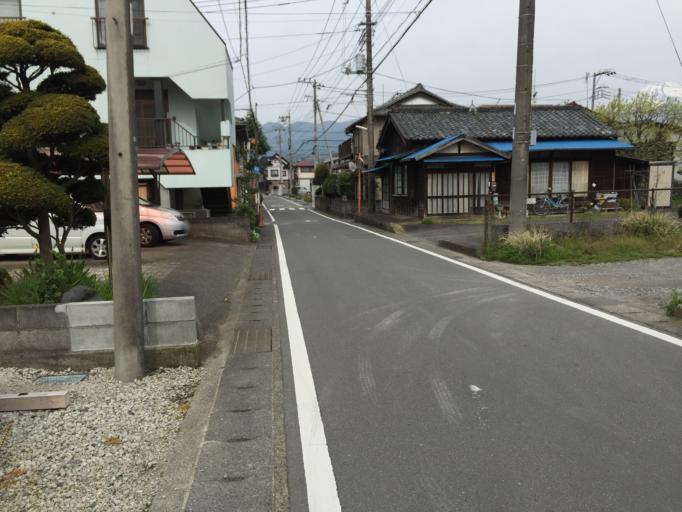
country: JP
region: Shizuoka
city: Mishima
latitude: 35.1716
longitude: 138.9150
